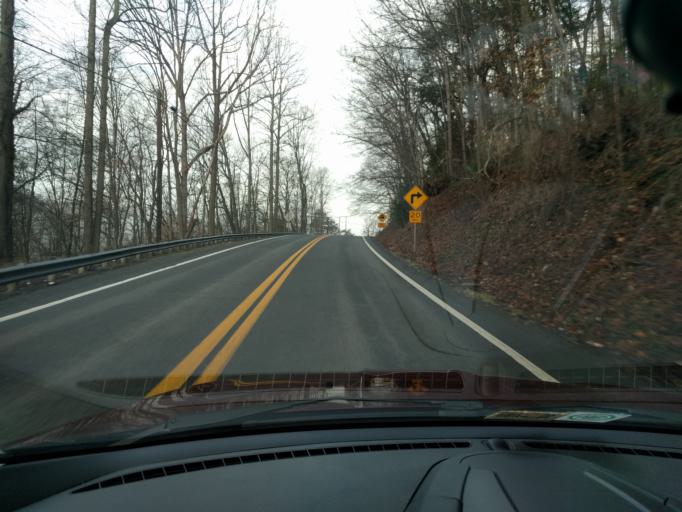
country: US
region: West Virginia
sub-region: Fayette County
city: Ansted
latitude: 38.1346
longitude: -81.1451
